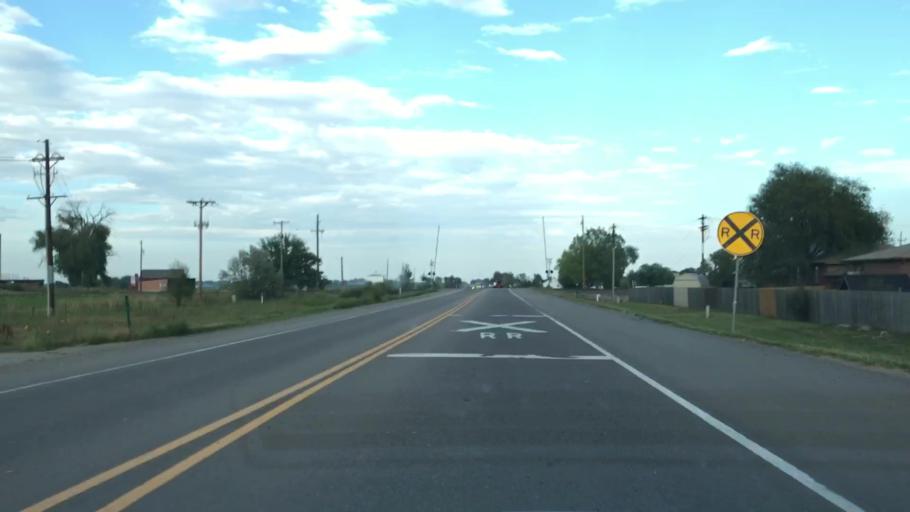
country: US
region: Colorado
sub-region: Boulder County
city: Longmont
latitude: 40.2032
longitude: -105.0947
